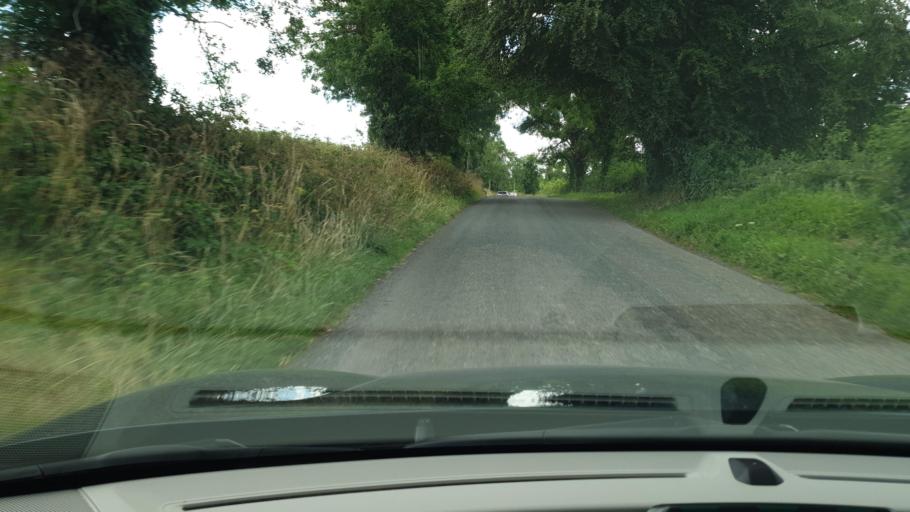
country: IE
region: Leinster
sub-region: An Mhi
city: Newtown Trim
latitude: 53.5450
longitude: -6.6907
